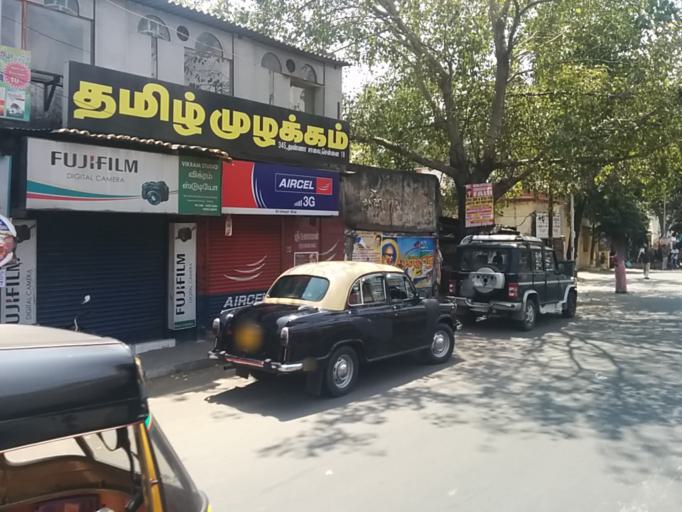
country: IN
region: Tamil Nadu
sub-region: Chennai
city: Chetput
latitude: 13.0478
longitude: 80.2493
